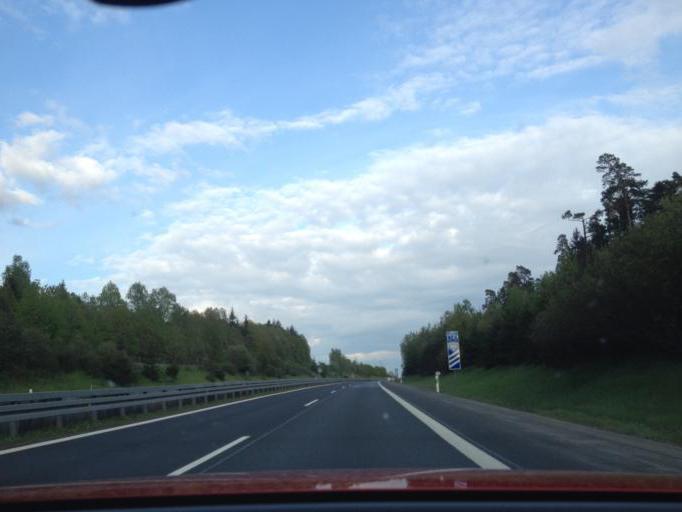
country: DE
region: Bavaria
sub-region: Upper Palatinate
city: Pechbrunn
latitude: 49.9524
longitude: 12.2018
